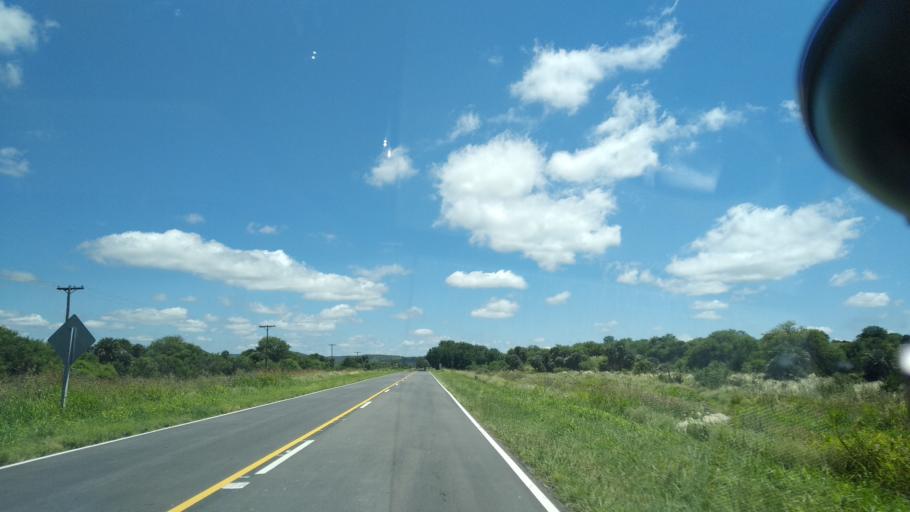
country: AR
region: Cordoba
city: Salsacate
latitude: -31.3794
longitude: -65.1005
